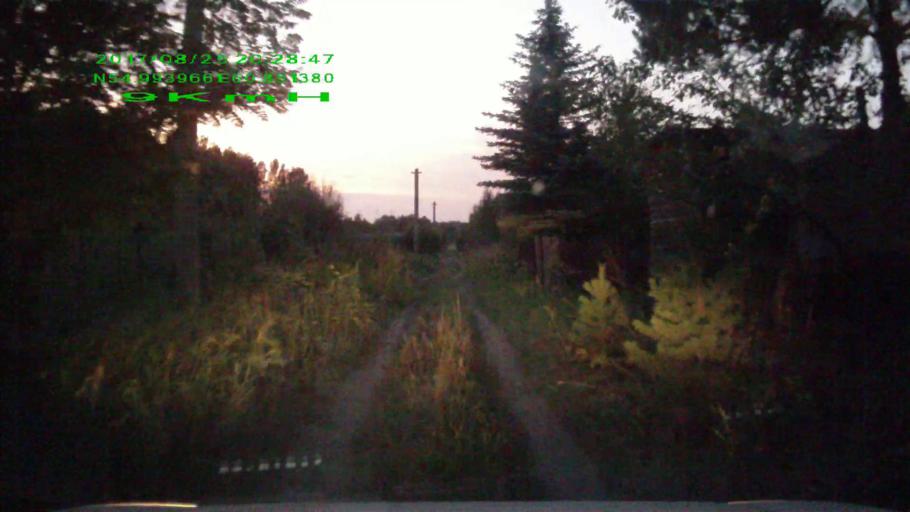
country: RU
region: Chelyabinsk
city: Timiryazevskiy
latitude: 54.9940
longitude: 60.8513
